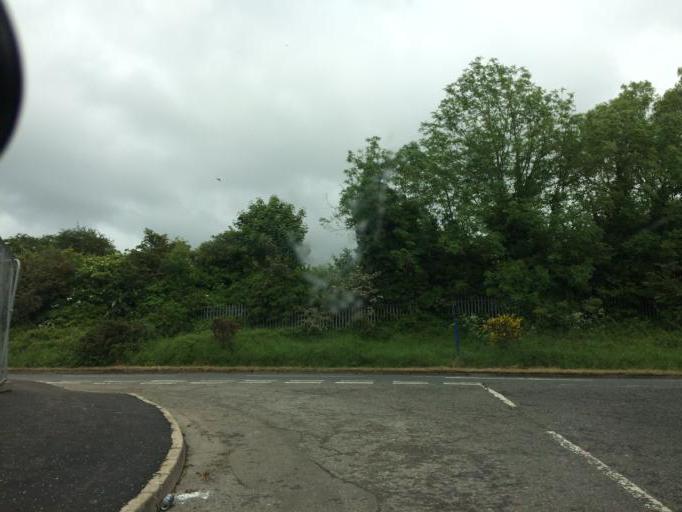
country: GB
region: Northern Ireland
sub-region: Antrim Borough
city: Antrim
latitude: 54.7120
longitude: -6.2105
